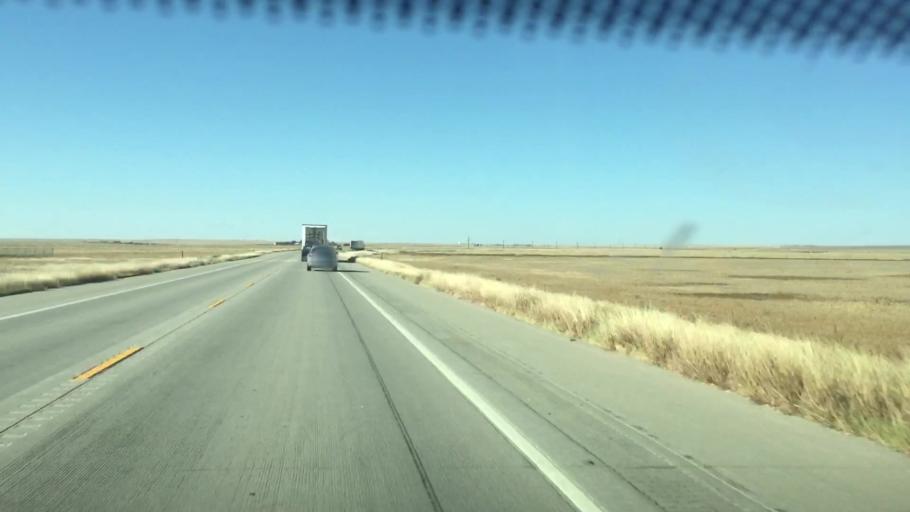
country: US
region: Colorado
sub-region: Kiowa County
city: Eads
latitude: 38.3715
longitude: -102.7278
